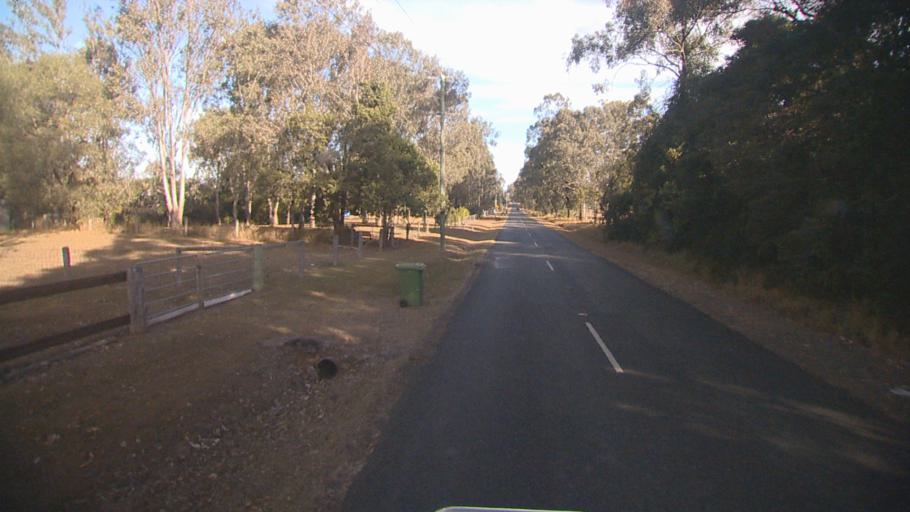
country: AU
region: Queensland
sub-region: Logan
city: Cedar Vale
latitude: -27.8676
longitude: 153.0115
